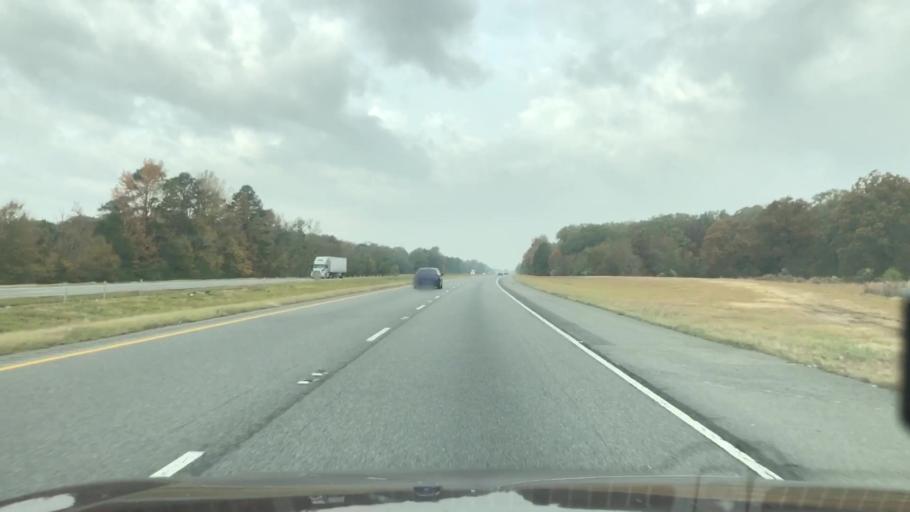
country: US
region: Louisiana
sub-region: Richland Parish
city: Delhi
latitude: 32.4461
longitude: -91.5447
